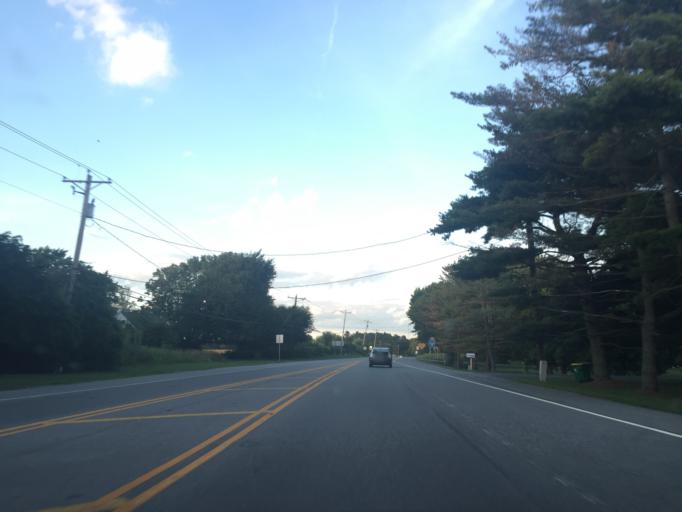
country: US
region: Delaware
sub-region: New Castle County
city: Middletown
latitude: 39.4563
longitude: -75.6710
